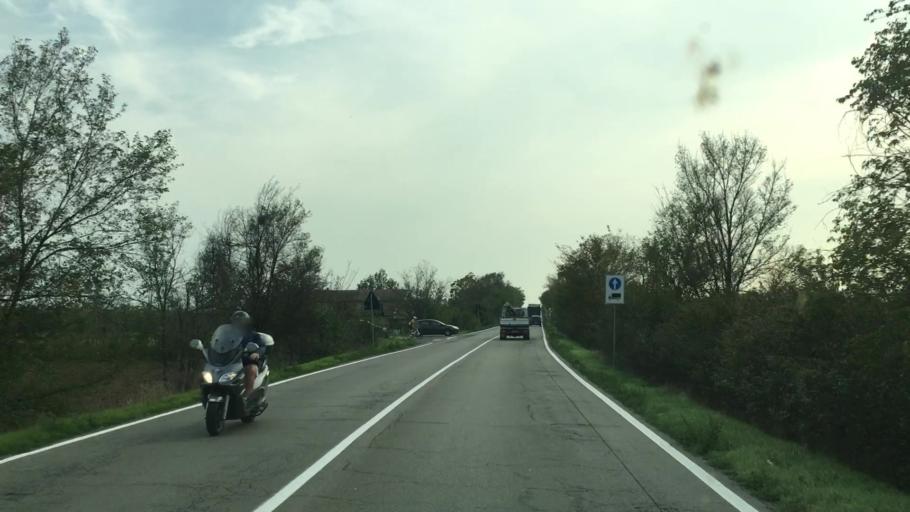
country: IT
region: Emilia-Romagna
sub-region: Provincia di Reggio Emilia
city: Calerno
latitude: 44.7548
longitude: 10.4953
